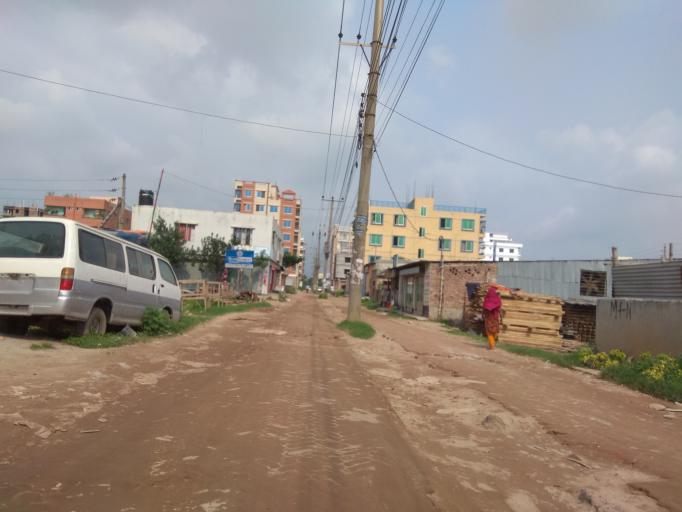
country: BD
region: Dhaka
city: Tungi
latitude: 23.8325
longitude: 90.3524
